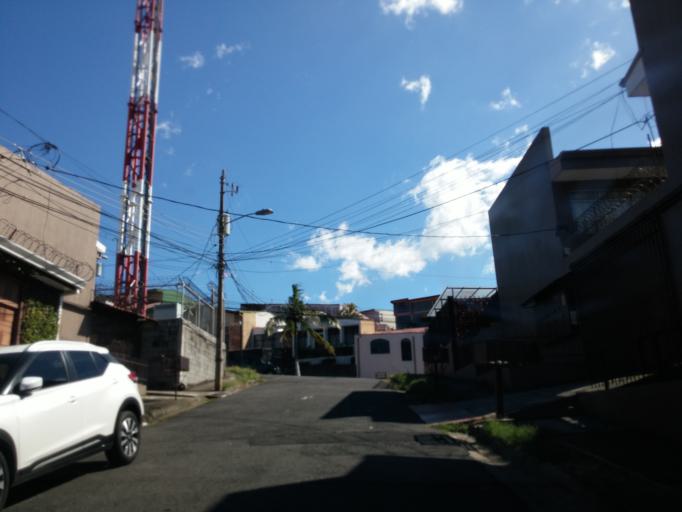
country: CR
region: San Jose
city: Colima
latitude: 9.9434
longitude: -84.0939
